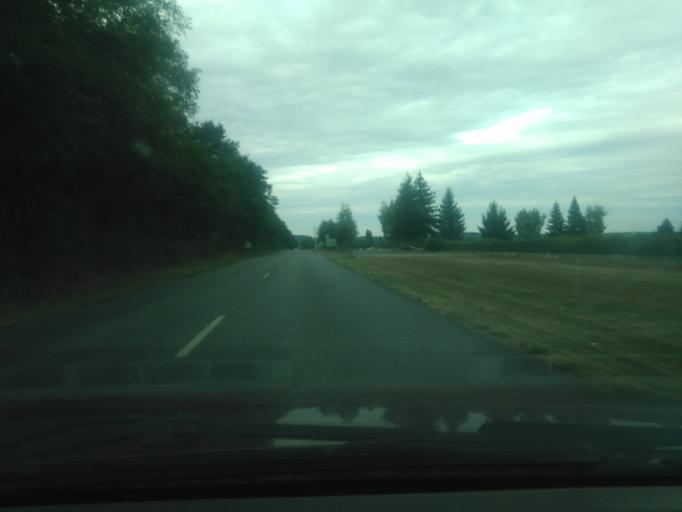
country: FR
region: Bourgogne
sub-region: Departement de la Nievre
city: Decize
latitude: 46.8106
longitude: 3.4482
